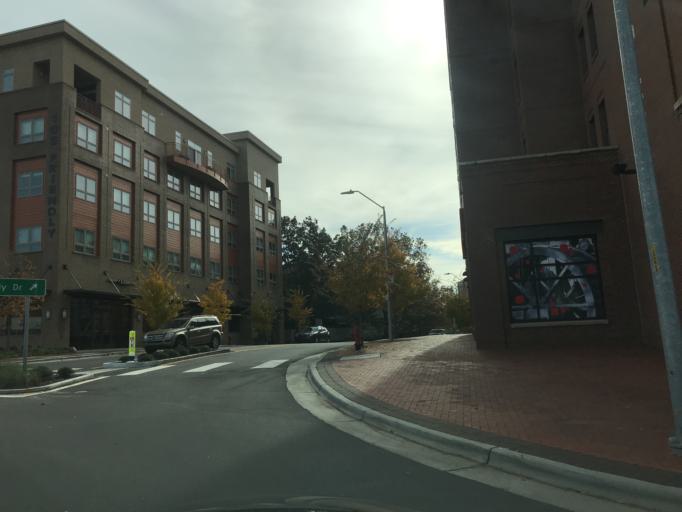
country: US
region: North Carolina
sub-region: Wake County
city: West Raleigh
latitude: 35.7895
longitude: -78.6760
